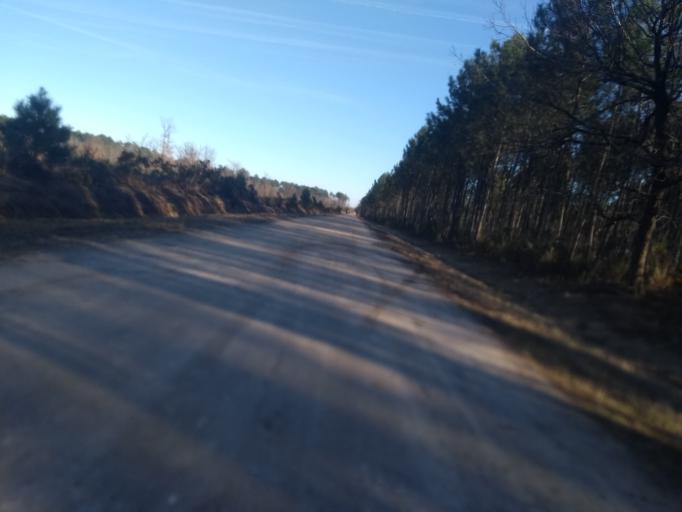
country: FR
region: Aquitaine
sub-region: Departement de la Gironde
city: Le Barp
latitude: 44.6156
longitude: -0.7908
